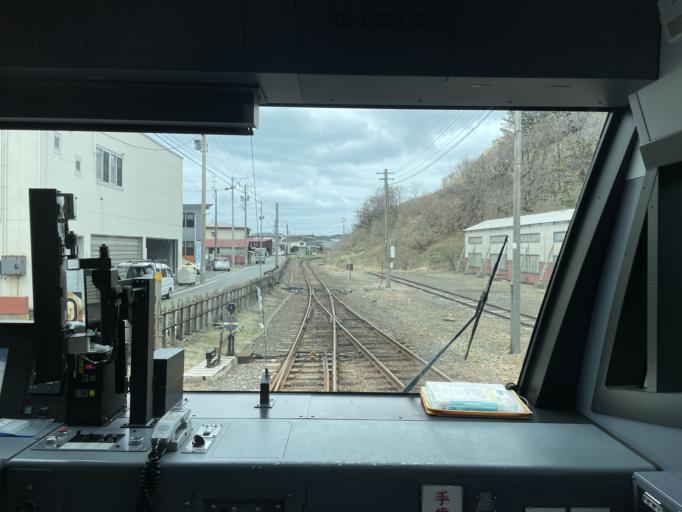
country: JP
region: Akita
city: Noshiromachi
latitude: 40.6510
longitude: 139.9298
